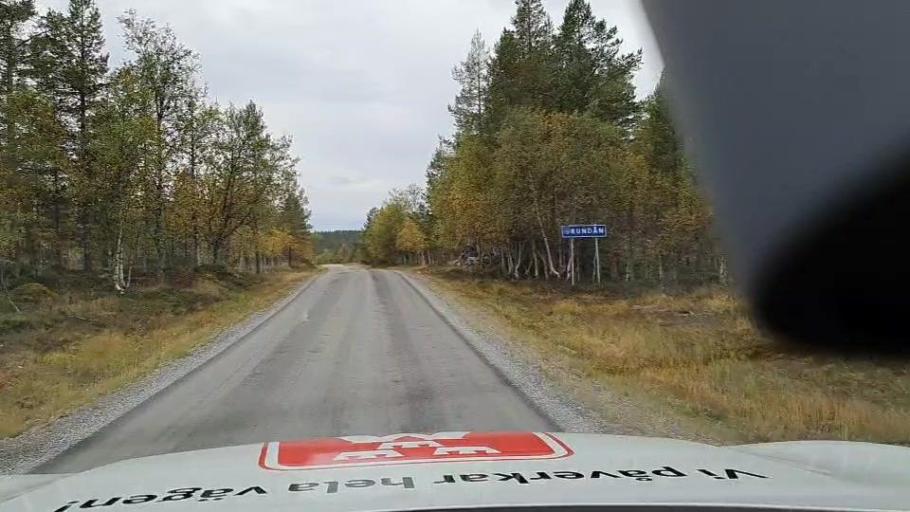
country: NO
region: Hedmark
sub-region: Engerdal
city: Engerdal
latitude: 62.0897
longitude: 12.7607
